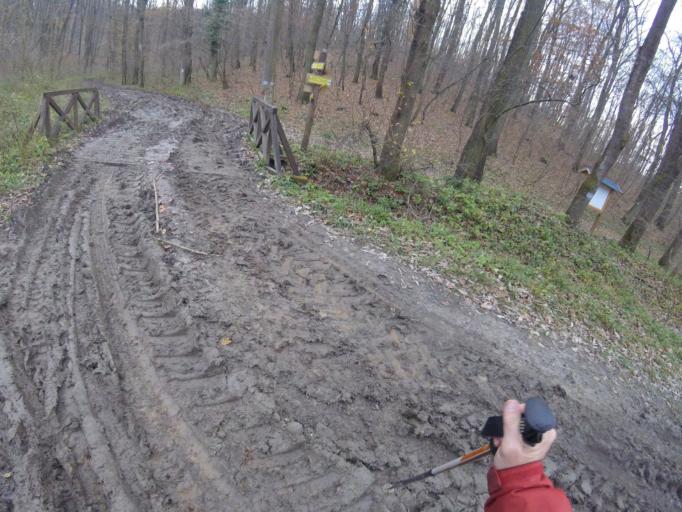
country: HU
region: Tolna
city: Szentgalpuszta
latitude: 46.3414
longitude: 18.6267
